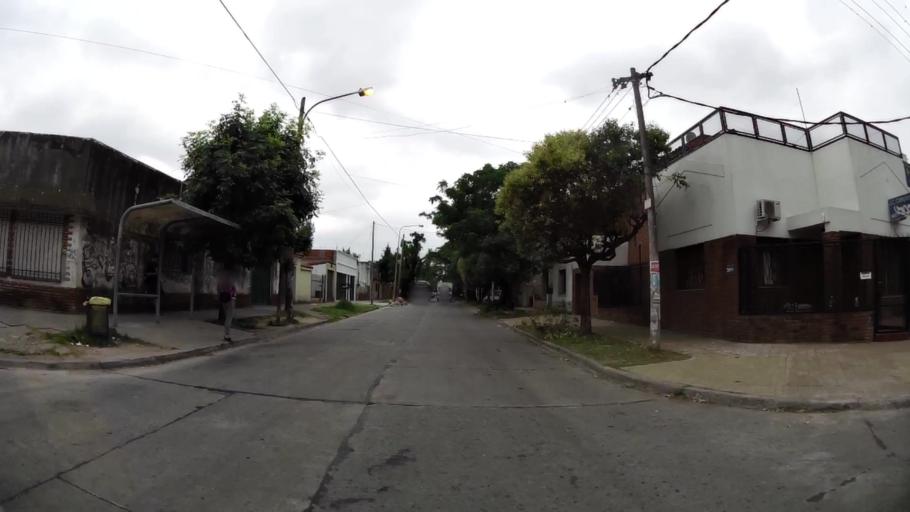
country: AR
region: Buenos Aires
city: San Justo
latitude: -34.7085
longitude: -58.5175
